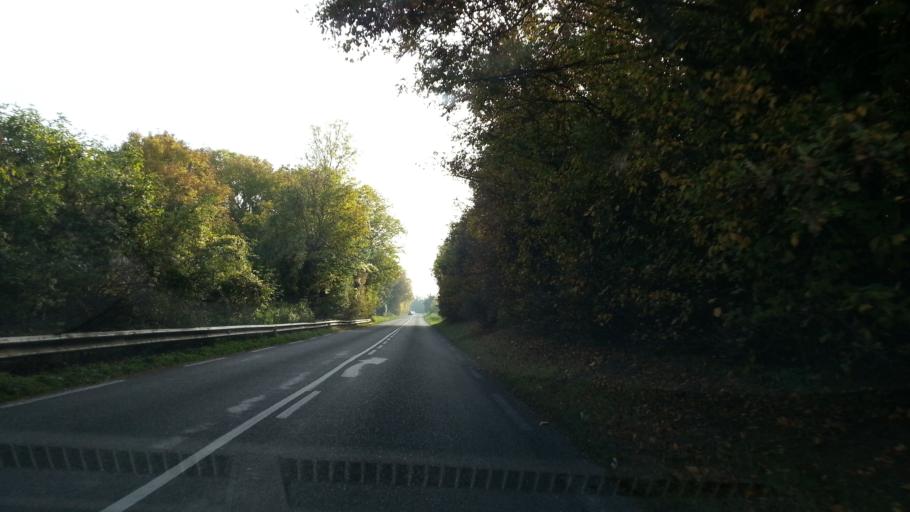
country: FR
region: Picardie
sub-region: Departement de l'Oise
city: Boran-sur-Oise
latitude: 49.1859
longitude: 2.3631
